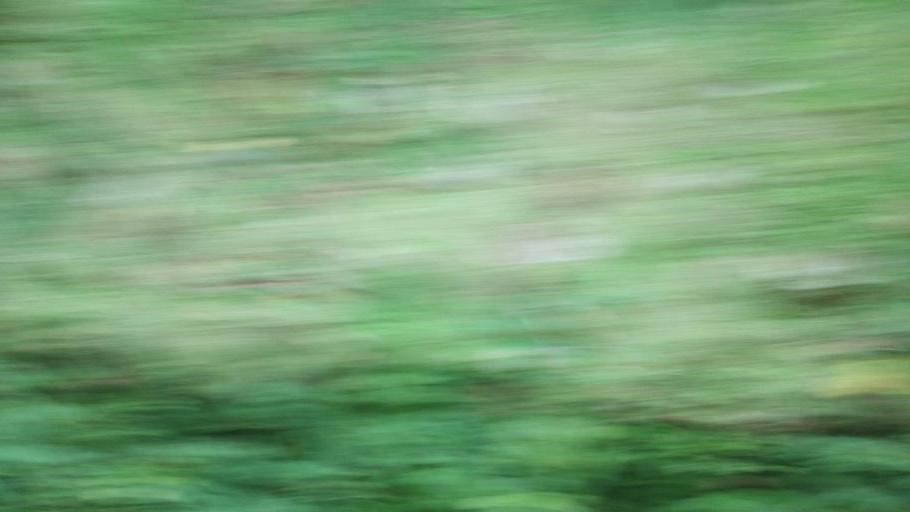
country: TW
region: Taipei
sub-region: Taipei
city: Banqiao
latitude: 24.9501
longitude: 121.4905
